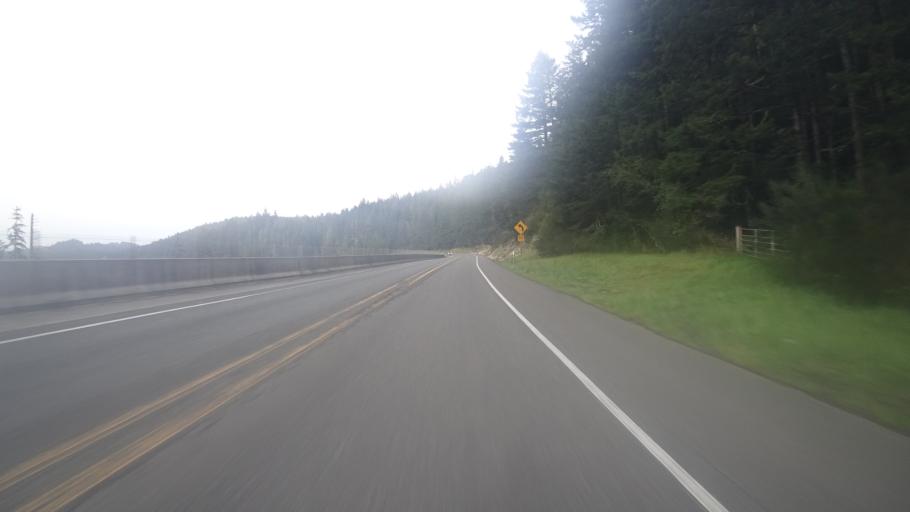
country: US
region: Oregon
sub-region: Coos County
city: Lakeside
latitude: 43.6453
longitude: -124.1897
